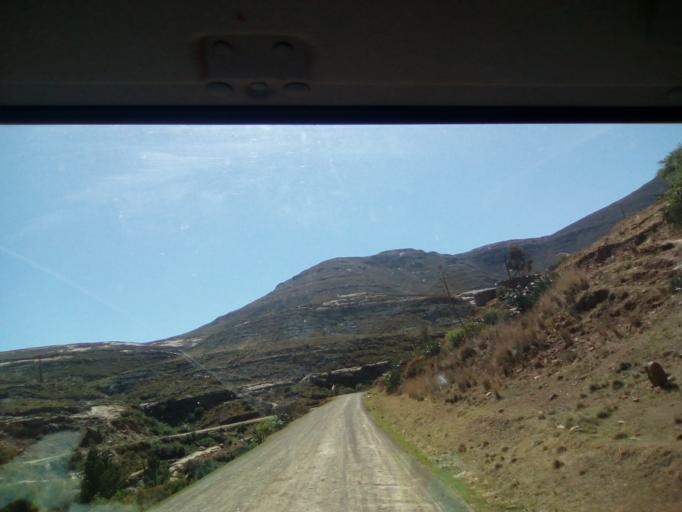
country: LS
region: Qacha's Nek
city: Qacha's Nek
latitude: -30.0425
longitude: 28.6597
